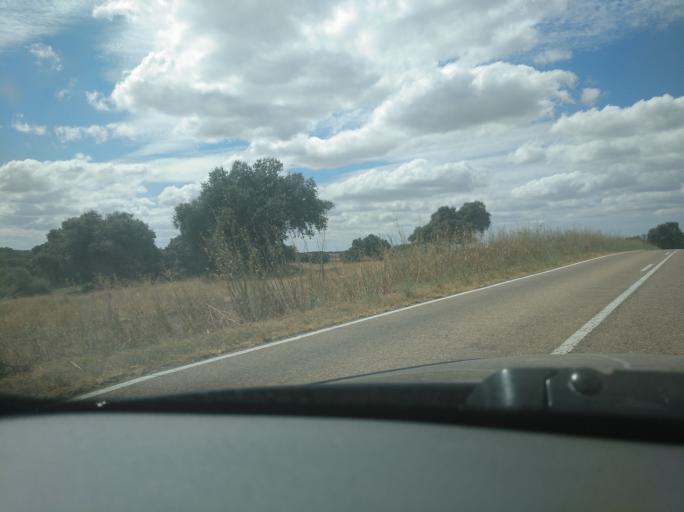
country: PT
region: Portalegre
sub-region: Arronches
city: Arronches
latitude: 39.0339
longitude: -7.4107
